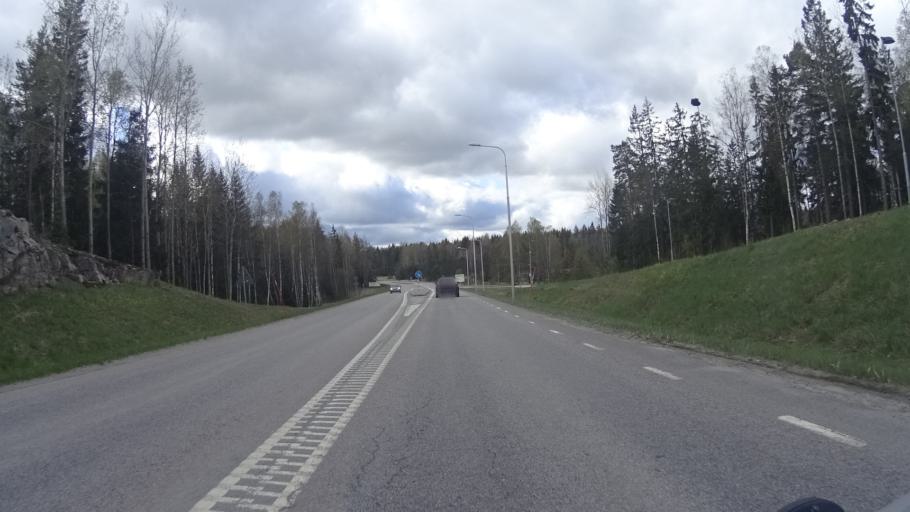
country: SE
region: Stockholm
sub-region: Botkyrka Kommun
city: Tullinge
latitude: 59.1955
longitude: 17.9292
